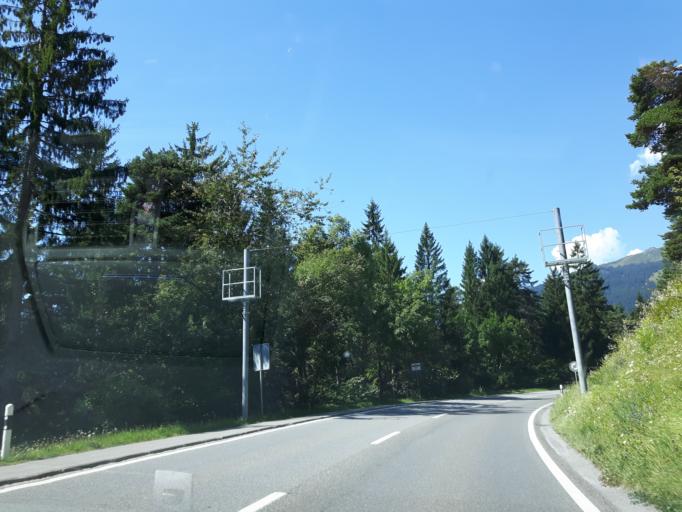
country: CH
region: Grisons
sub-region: Imboden District
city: Flims
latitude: 46.8247
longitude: 9.2805
